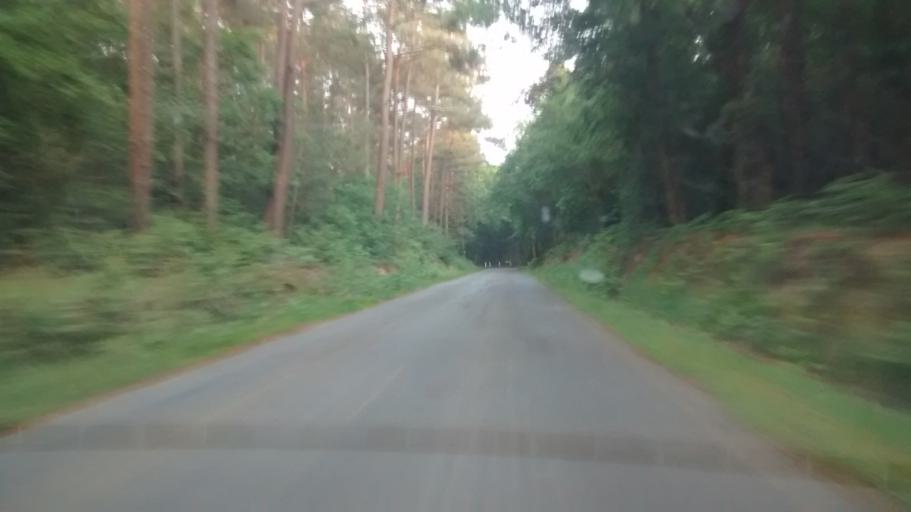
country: FR
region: Brittany
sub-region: Departement d'Ille-et-Vilaine
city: Paimpont
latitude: 47.9999
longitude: -2.1495
